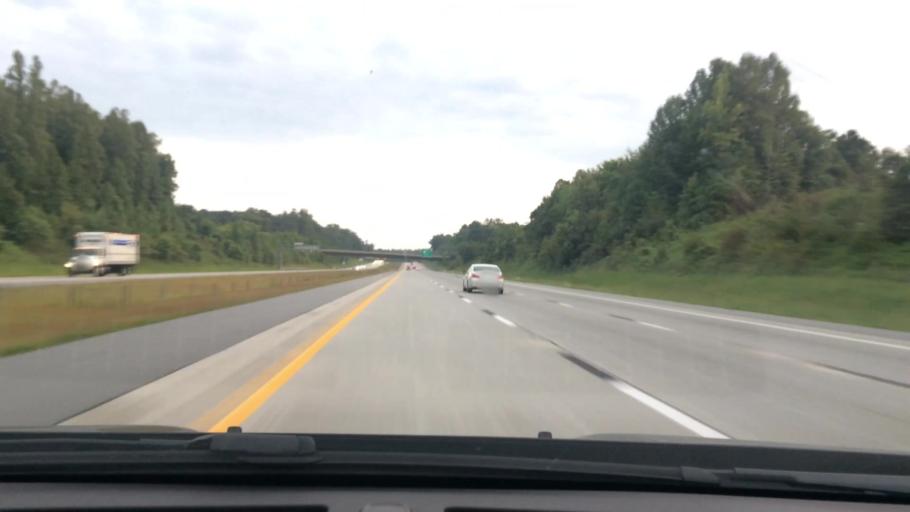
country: US
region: North Carolina
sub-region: Guilford County
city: Forest Oaks
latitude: 36.0163
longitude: -79.7352
